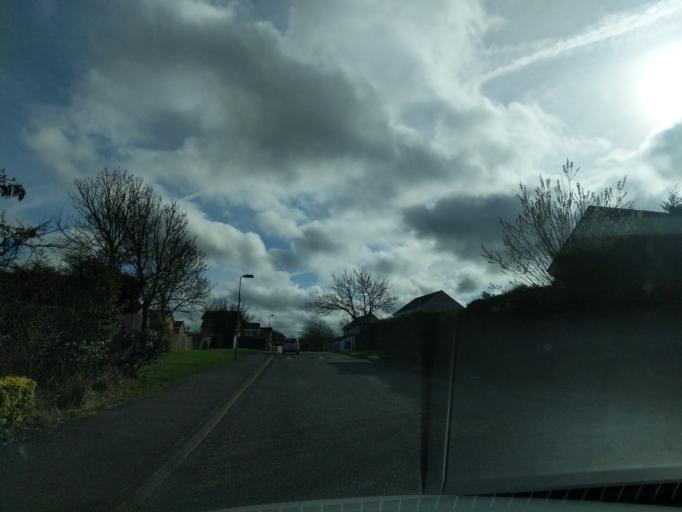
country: GB
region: Scotland
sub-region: Edinburgh
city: Queensferry
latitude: 55.9872
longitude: -3.4092
